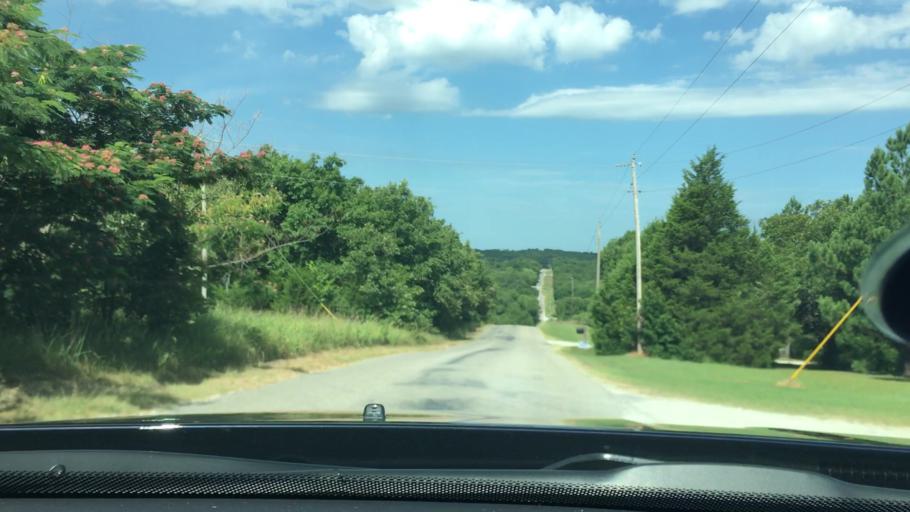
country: US
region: Oklahoma
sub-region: Pontotoc County
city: Ada
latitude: 34.7636
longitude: -96.5689
